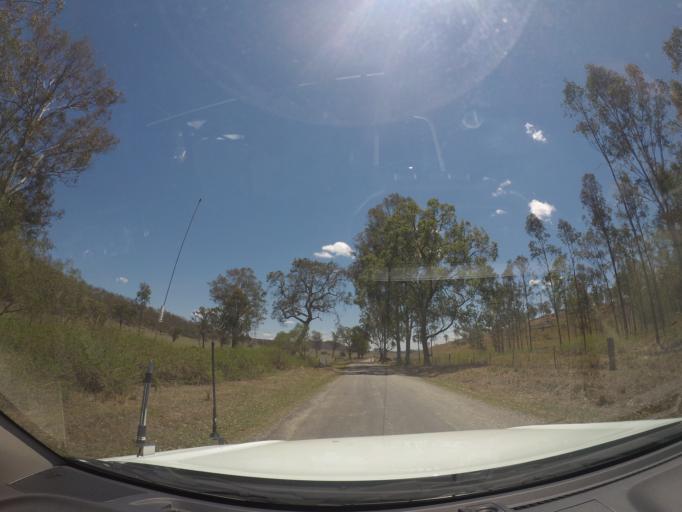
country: AU
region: Queensland
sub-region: Ipswich
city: Redbank Plains
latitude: -27.7535
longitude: 152.8344
